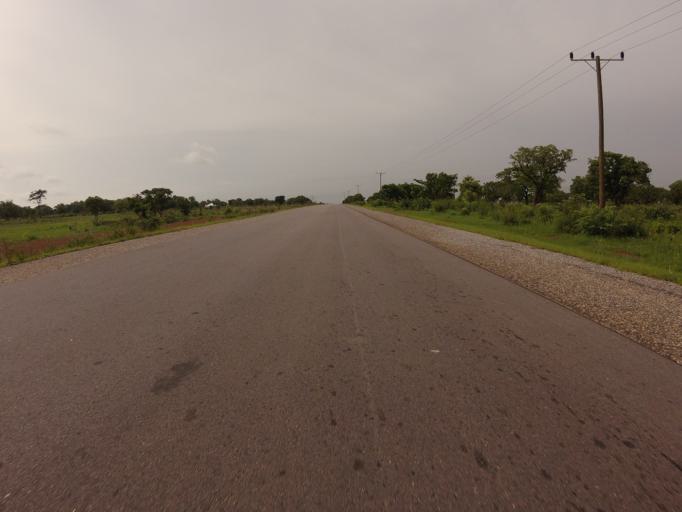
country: GH
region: Northern
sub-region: Yendi
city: Yendi
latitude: 9.6149
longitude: -0.0473
